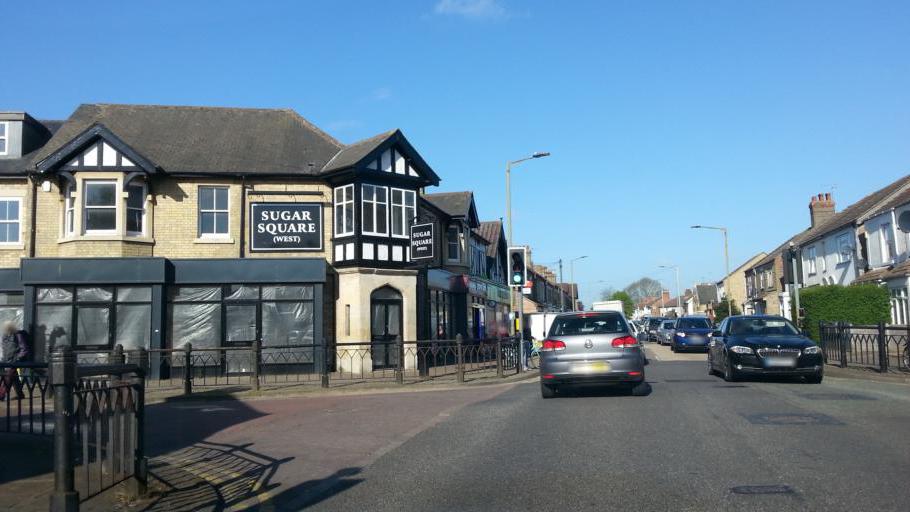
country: GB
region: England
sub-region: Peterborough
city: Peterborough
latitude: 52.5785
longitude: -0.2586
